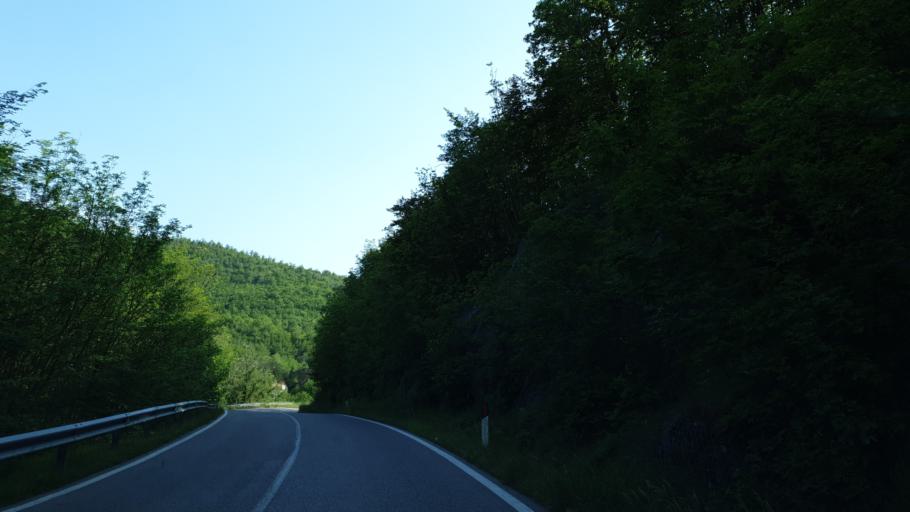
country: IT
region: Tuscany
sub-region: Province of Arezzo
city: Soci
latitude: 43.7626
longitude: 11.8353
